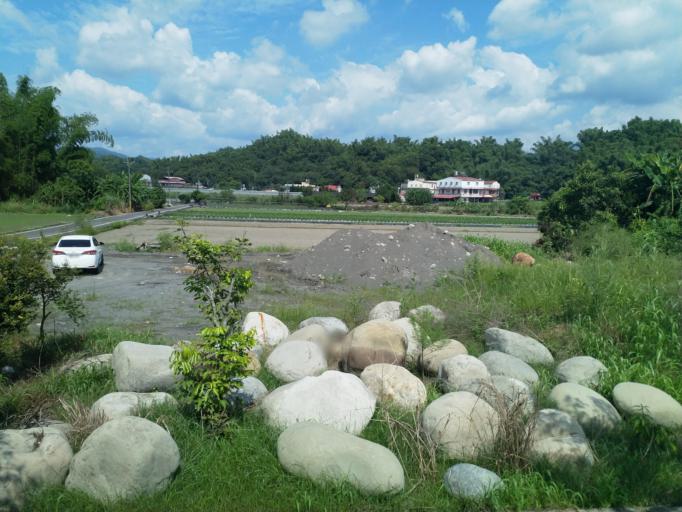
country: TW
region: Taiwan
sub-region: Pingtung
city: Pingtung
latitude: 22.8813
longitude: 120.5598
